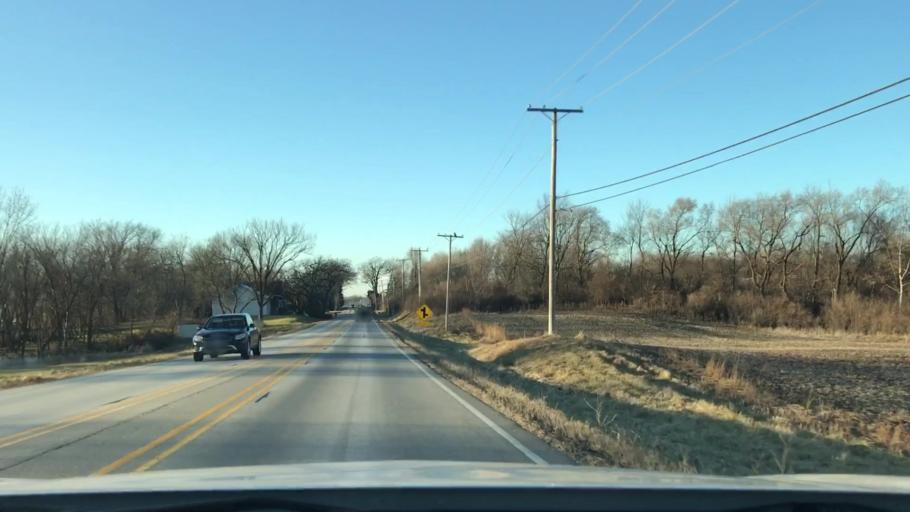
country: US
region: Illinois
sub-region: Kane County
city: Gilberts
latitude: 42.0807
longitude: -88.3822
